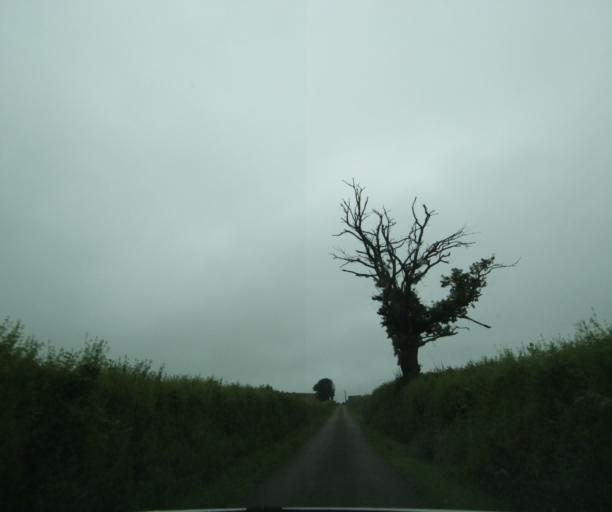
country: FR
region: Bourgogne
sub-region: Departement de Saone-et-Loire
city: Charolles
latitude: 46.3892
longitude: 4.1982
